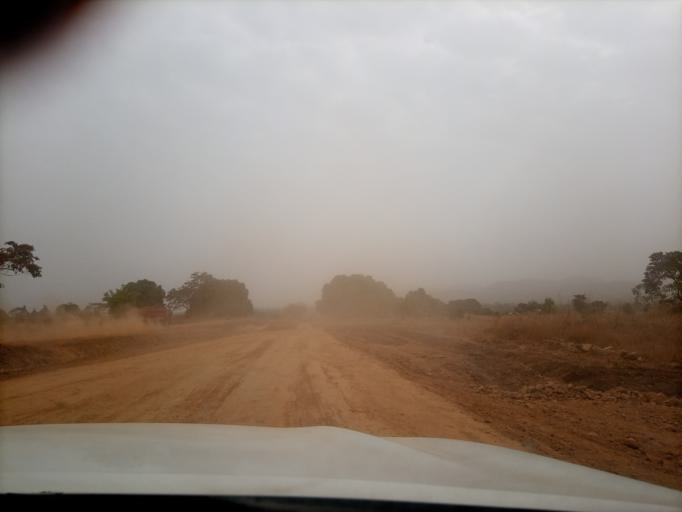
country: ET
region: Oromiya
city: Mendi
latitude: 10.2066
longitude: 35.0770
